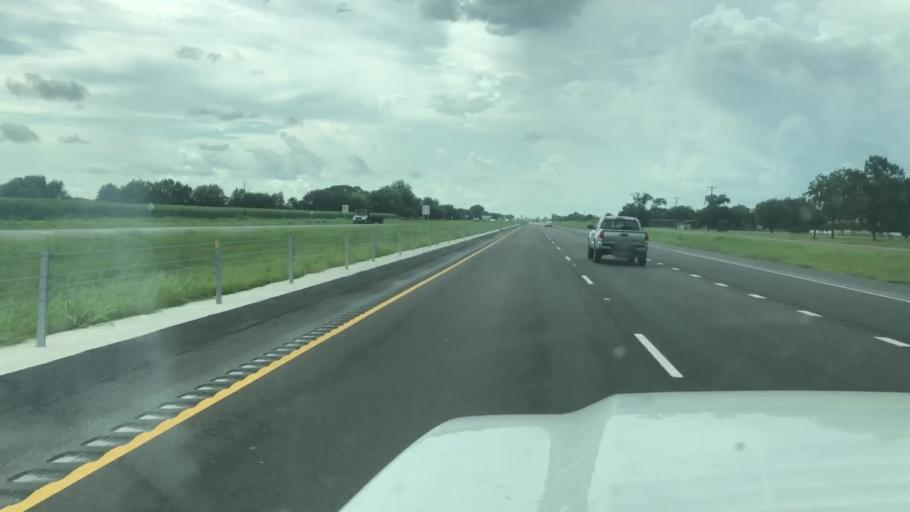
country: US
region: Louisiana
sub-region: Iberia Parish
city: Jeanerette
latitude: 29.8695
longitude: -91.6394
